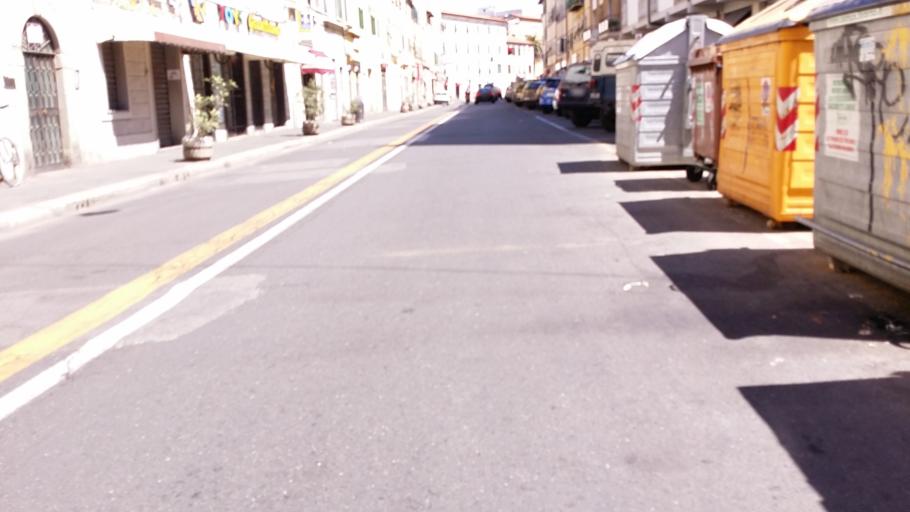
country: IT
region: Tuscany
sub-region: Provincia di Livorno
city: Livorno
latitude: 43.5555
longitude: 10.3159
